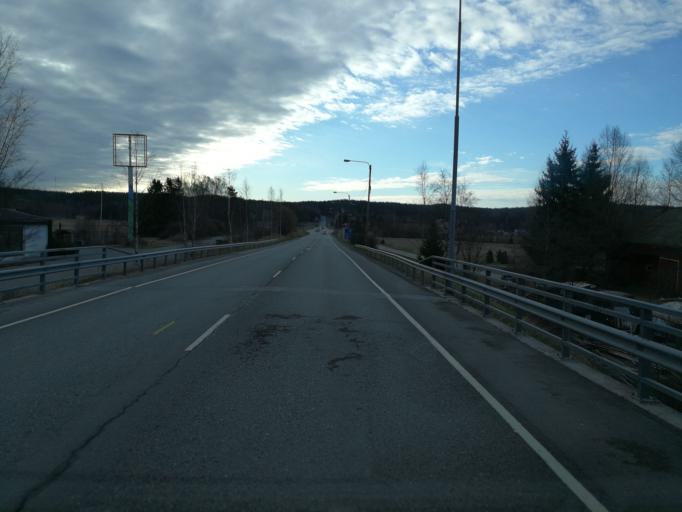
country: FI
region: Varsinais-Suomi
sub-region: Turku
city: Paimio
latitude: 60.4216
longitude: 22.6551
